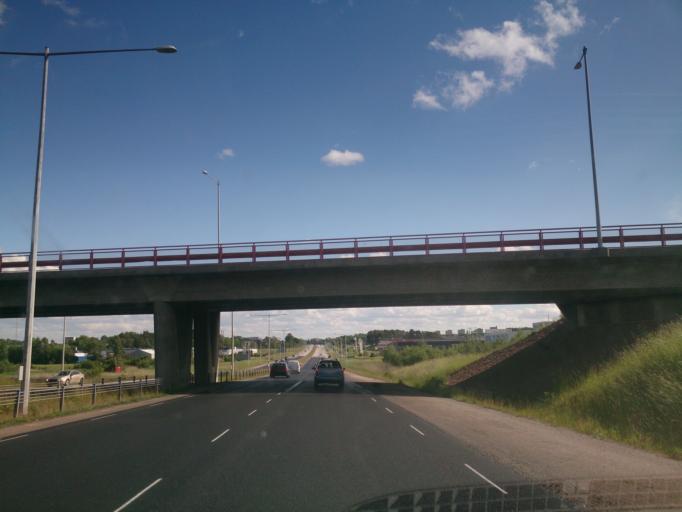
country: SE
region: OEstergoetland
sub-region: Norrkopings Kommun
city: Norrkoping
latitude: 58.6270
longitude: 16.1583
